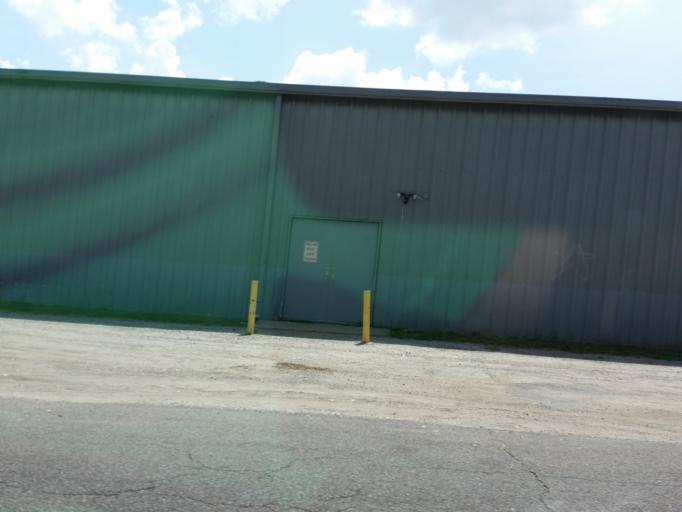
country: US
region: Mississippi
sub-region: Lauderdale County
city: Meridian
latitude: 32.3756
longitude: -88.7207
